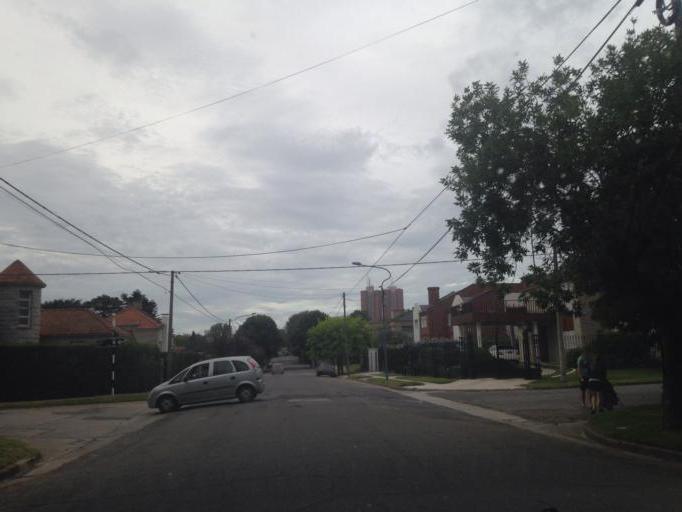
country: AR
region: Buenos Aires
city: Mar del Plata
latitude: -38.0242
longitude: -57.5386
